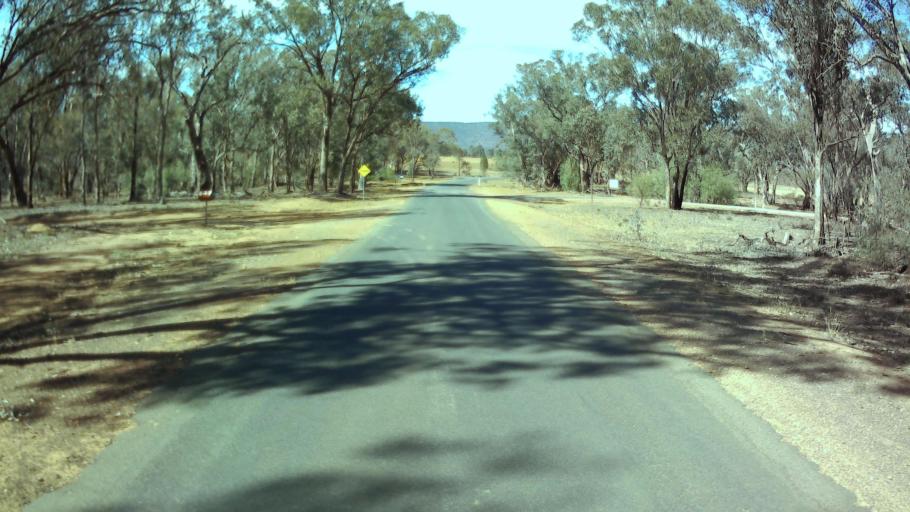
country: AU
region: New South Wales
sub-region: Weddin
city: Grenfell
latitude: -33.9389
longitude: 148.0795
